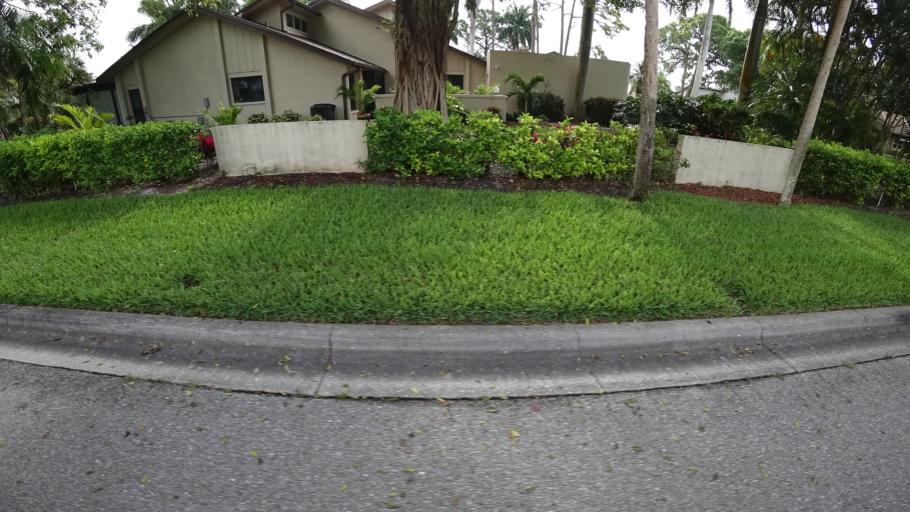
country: US
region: Florida
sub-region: Manatee County
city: Bayshore Gardens
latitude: 27.4337
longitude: -82.6082
